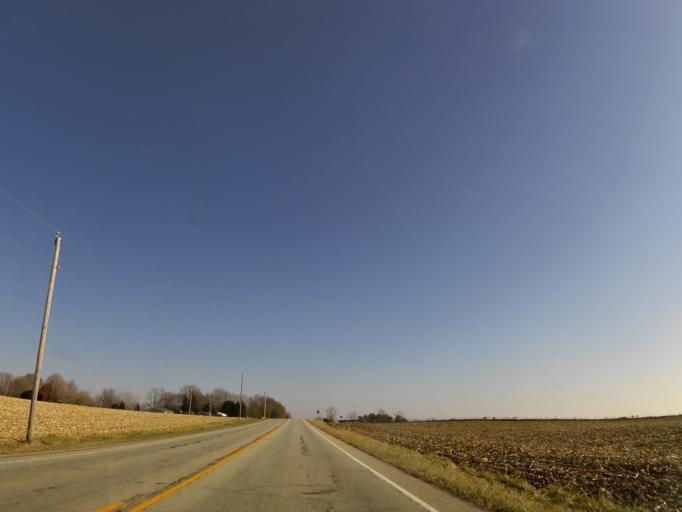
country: US
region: Indiana
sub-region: Fayette County
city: Connersville
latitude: 39.6300
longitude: -85.2457
